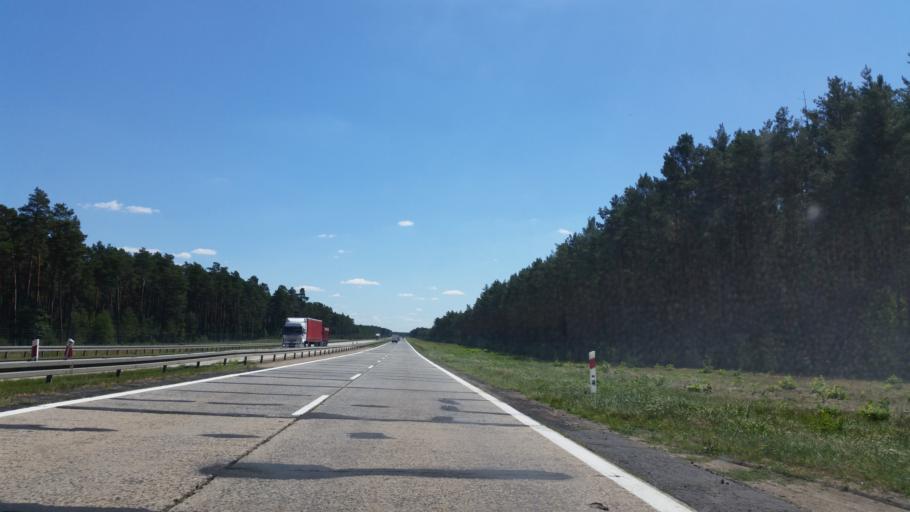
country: PL
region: Lower Silesian Voivodeship
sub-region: Powiat boleslawiecki
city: Boleslawiec
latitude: 51.3901
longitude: 15.5359
